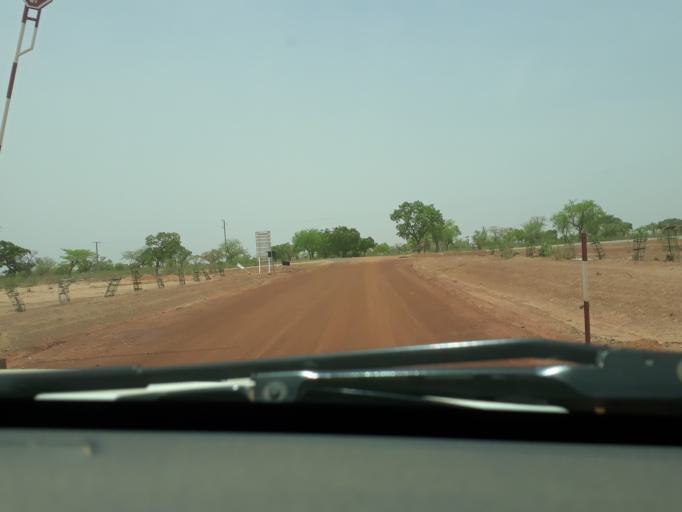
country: BF
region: Plateau-Central
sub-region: Province d'Oubritenga
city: Ziniare
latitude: 12.5789
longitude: -1.3312
